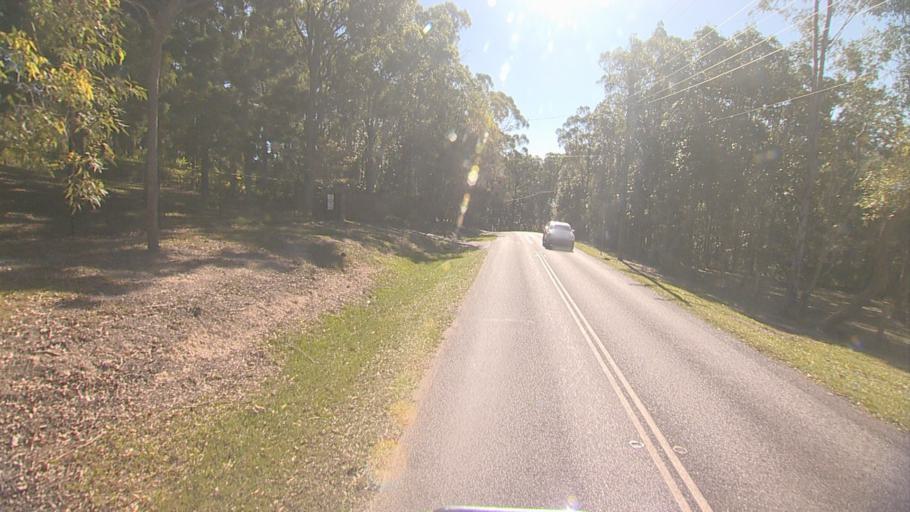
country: AU
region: Queensland
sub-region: Logan
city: Springwood
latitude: -27.5986
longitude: 153.1646
